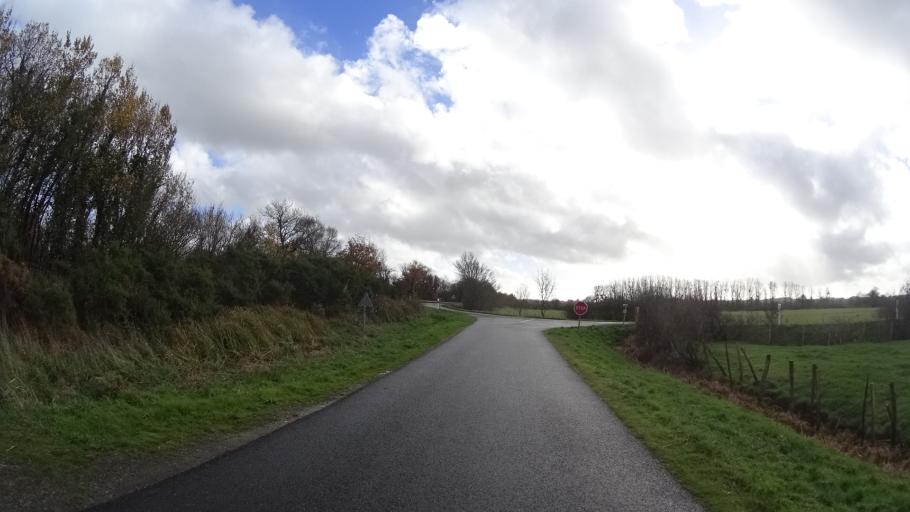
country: FR
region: Brittany
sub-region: Departement du Morbihan
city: Rieux
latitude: 47.5822
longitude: -2.0807
